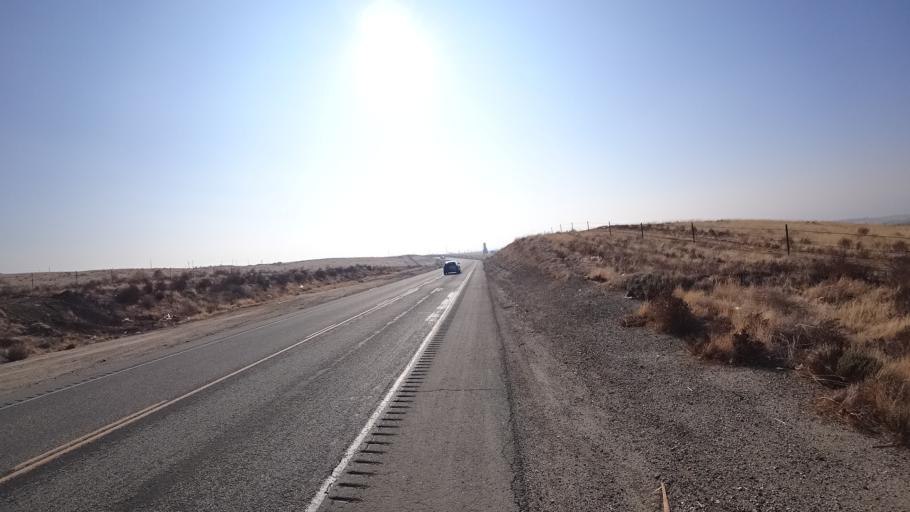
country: US
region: California
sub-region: Kern County
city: Lamont
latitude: 35.3826
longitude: -118.8508
